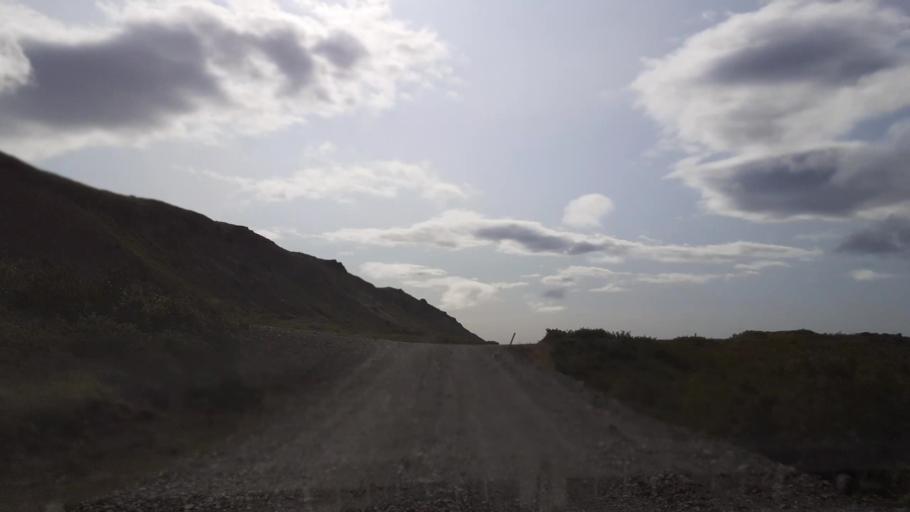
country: IS
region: East
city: Hoefn
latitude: 64.4300
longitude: -14.8873
